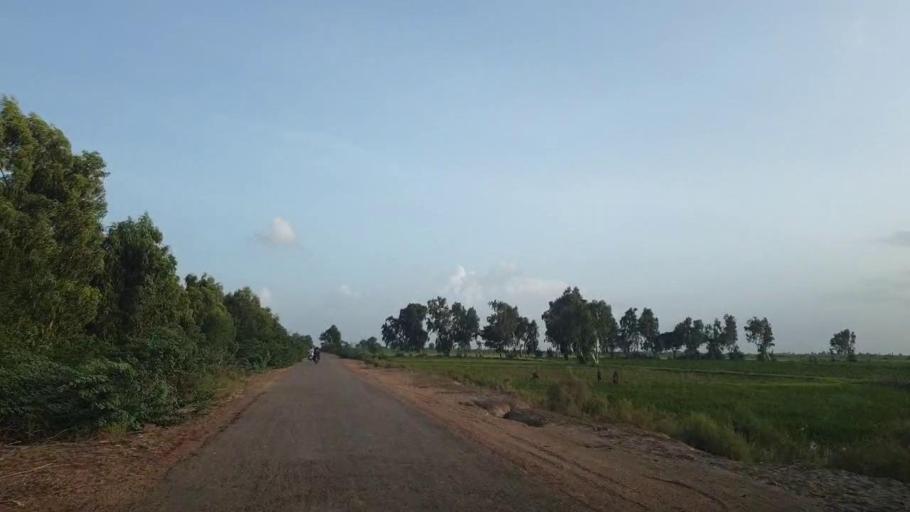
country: PK
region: Sindh
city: Kadhan
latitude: 24.6151
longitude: 69.1158
